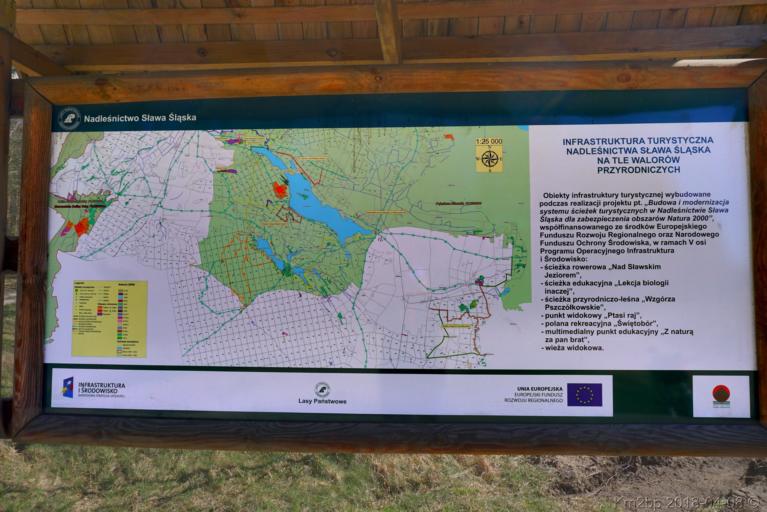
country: PL
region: Lubusz
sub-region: Powiat nowosolski
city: Kolsko
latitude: 51.9246
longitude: 15.9500
